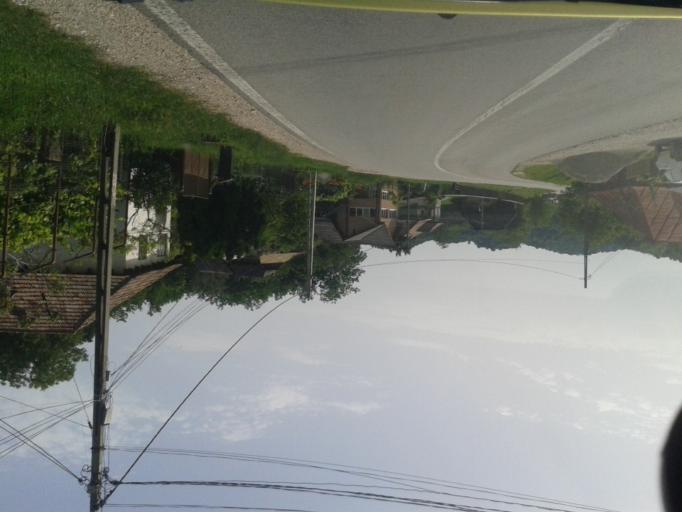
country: RO
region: Valcea
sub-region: Comuna Costesti
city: Costesti
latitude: 45.1377
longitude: 24.0795
